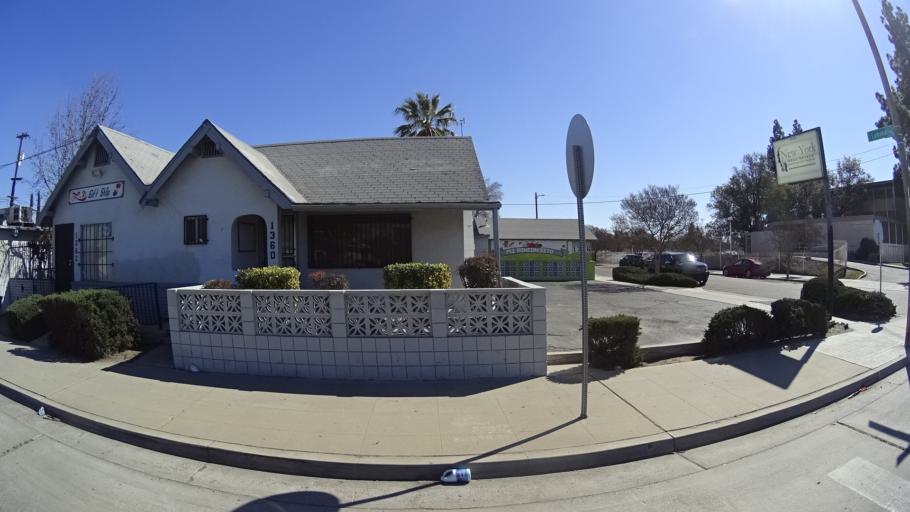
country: US
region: California
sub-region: Fresno County
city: Fresno
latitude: 36.7605
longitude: -119.7815
